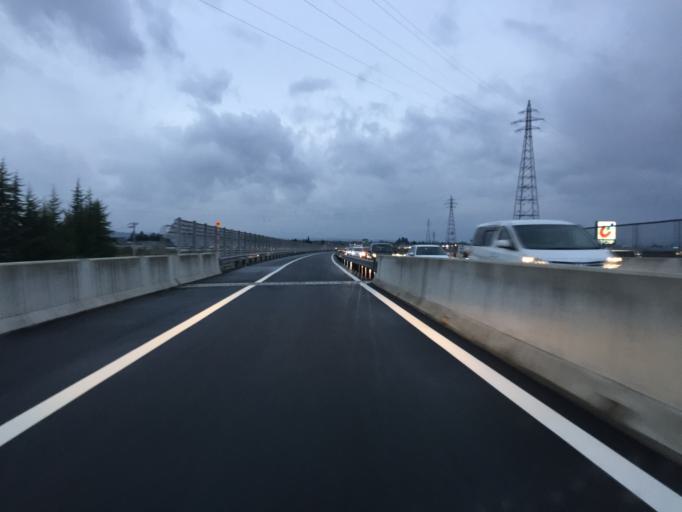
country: JP
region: Yamagata
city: Yonezawa
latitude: 37.9427
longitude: 140.1205
